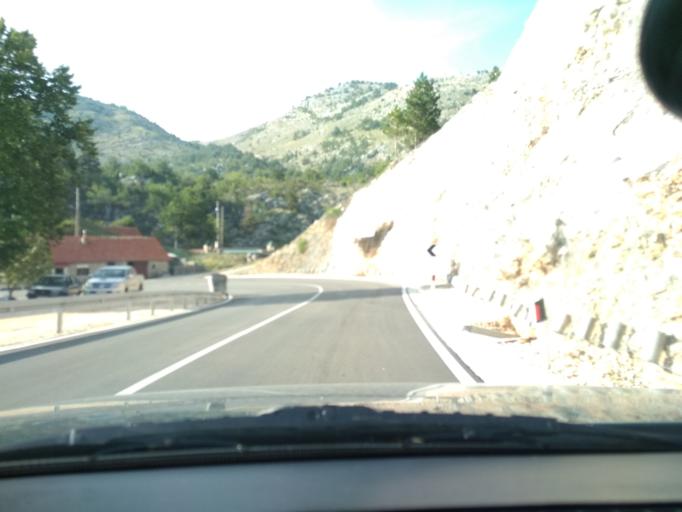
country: ME
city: Dobrota
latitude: 42.4375
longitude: 18.8293
